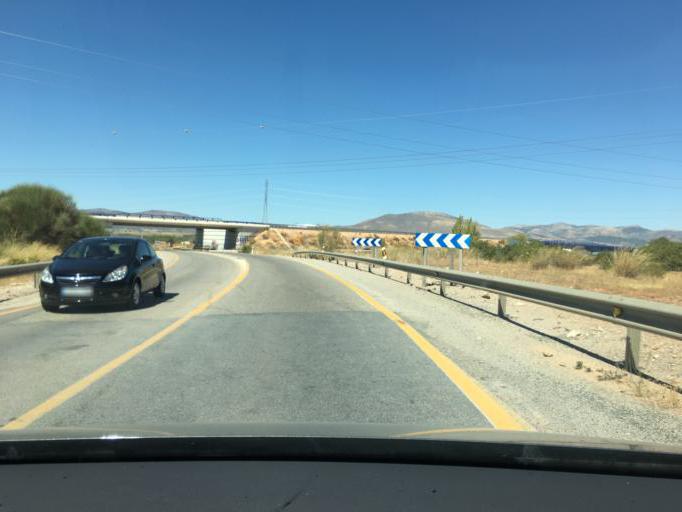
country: ES
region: Andalusia
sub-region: Provincia de Granada
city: Albolote
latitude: 37.2626
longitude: -3.6600
